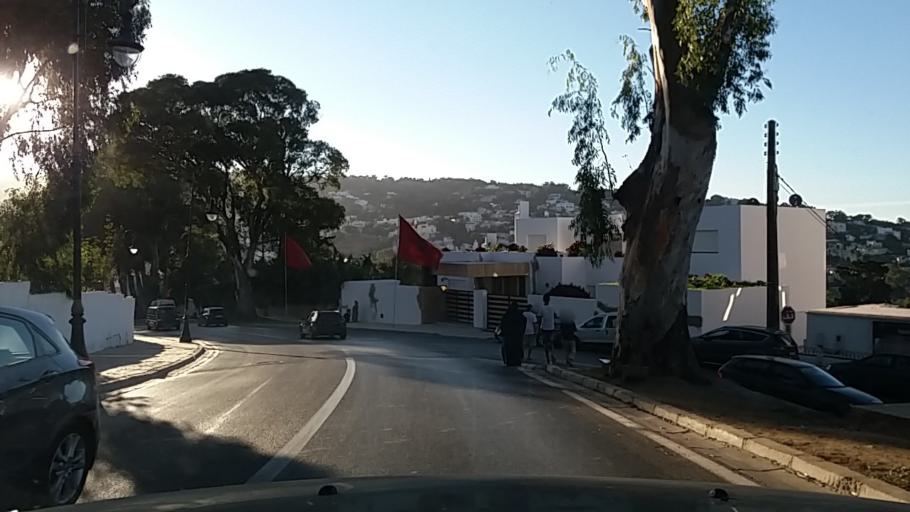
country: MA
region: Tanger-Tetouan
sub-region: Tanger-Assilah
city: Tangier
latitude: 35.7802
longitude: -5.8341
